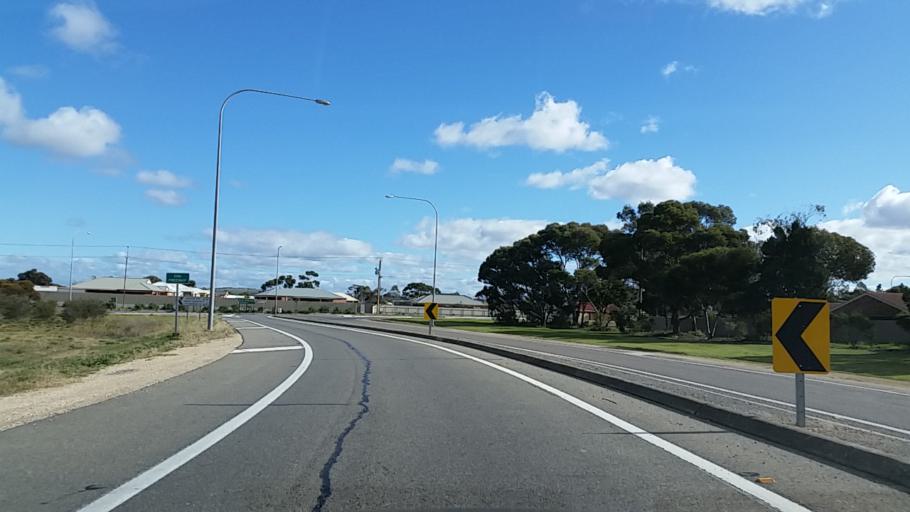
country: AU
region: South Australia
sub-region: Murray Bridge
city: Murray Bridge
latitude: -35.1488
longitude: 139.2878
